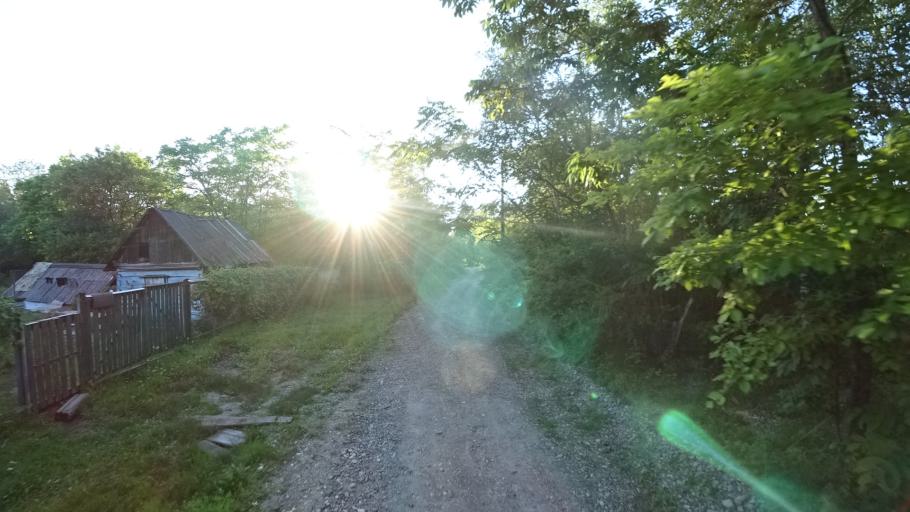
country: RU
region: Khabarovsk Krai
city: Khor
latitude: 47.8537
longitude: 135.0046
